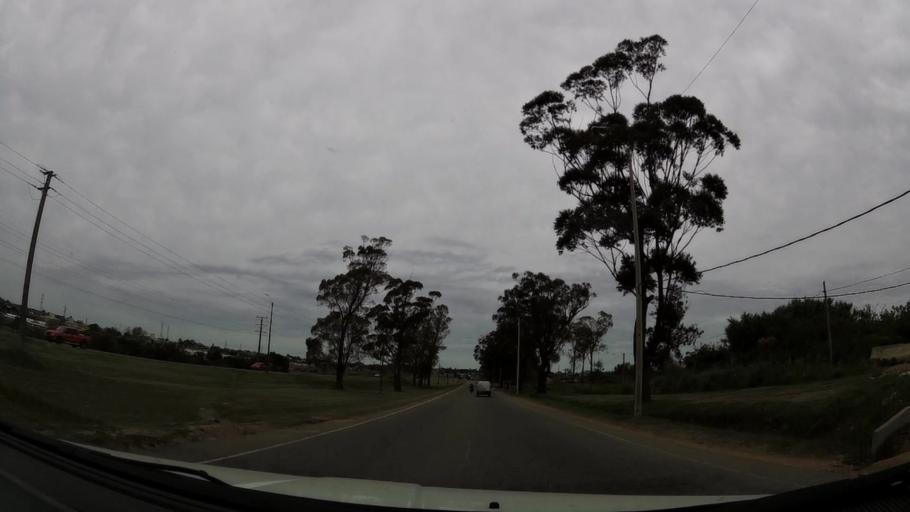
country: UY
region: Maldonado
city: Maldonado
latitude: -34.8851
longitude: -54.9518
